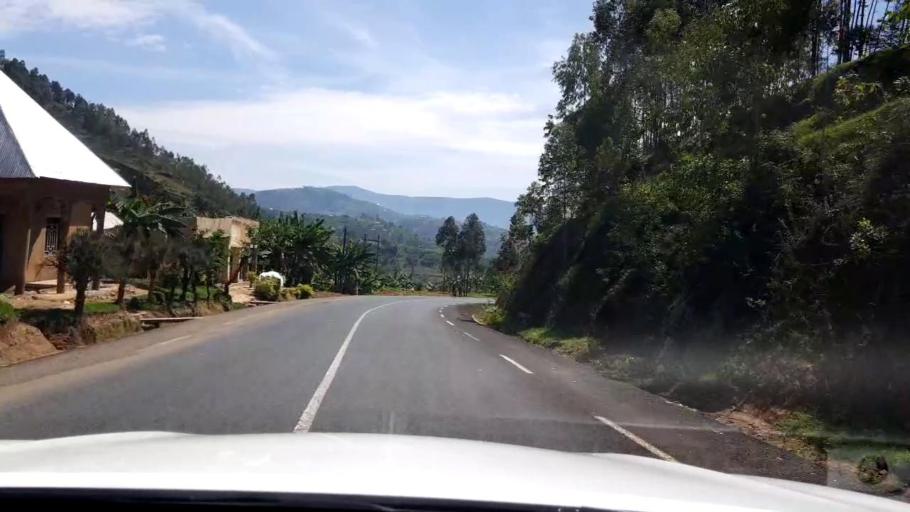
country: RW
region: Southern Province
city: Gitarama
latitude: -1.9187
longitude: 29.6308
